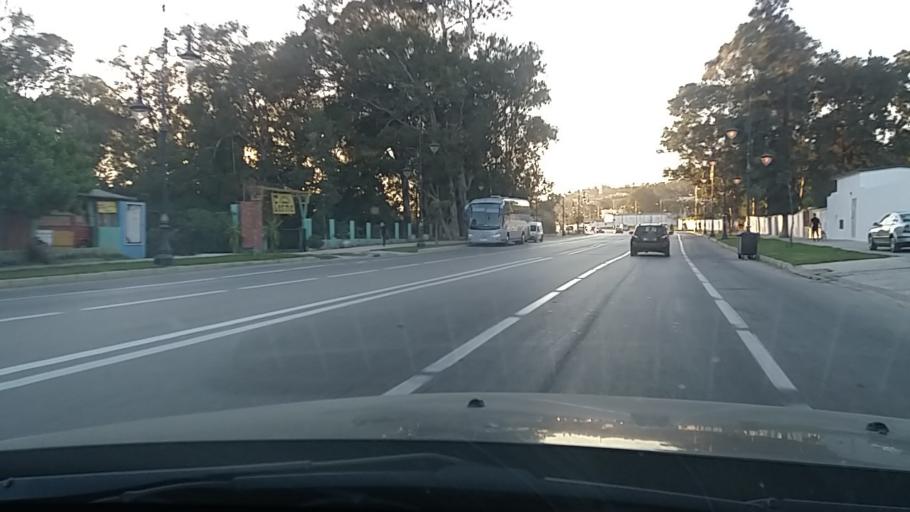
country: MA
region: Tanger-Tetouan
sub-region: Tanger-Assilah
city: Boukhalef
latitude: 35.7417
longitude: -5.8802
